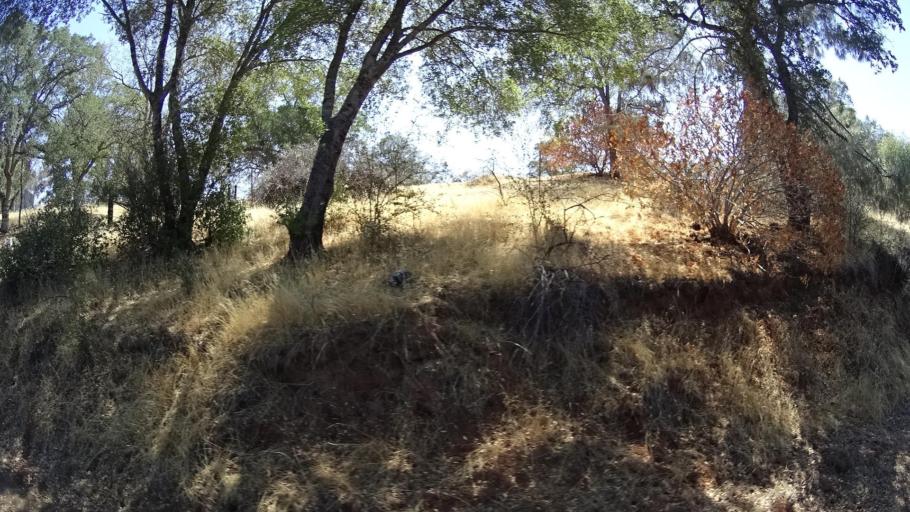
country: US
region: California
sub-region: Mariposa County
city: Mariposa
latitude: 37.4647
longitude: -119.9156
